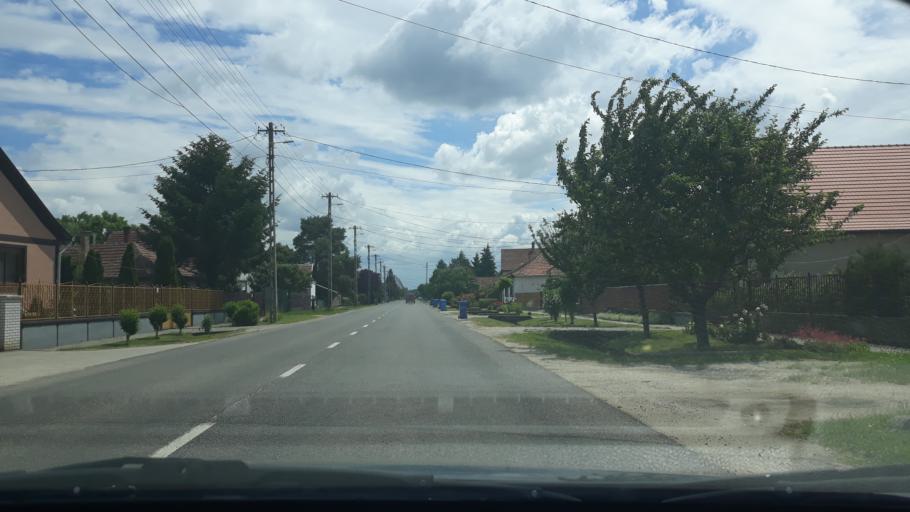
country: HU
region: Hajdu-Bihar
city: Biharkeresztes
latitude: 47.1317
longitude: 21.7220
